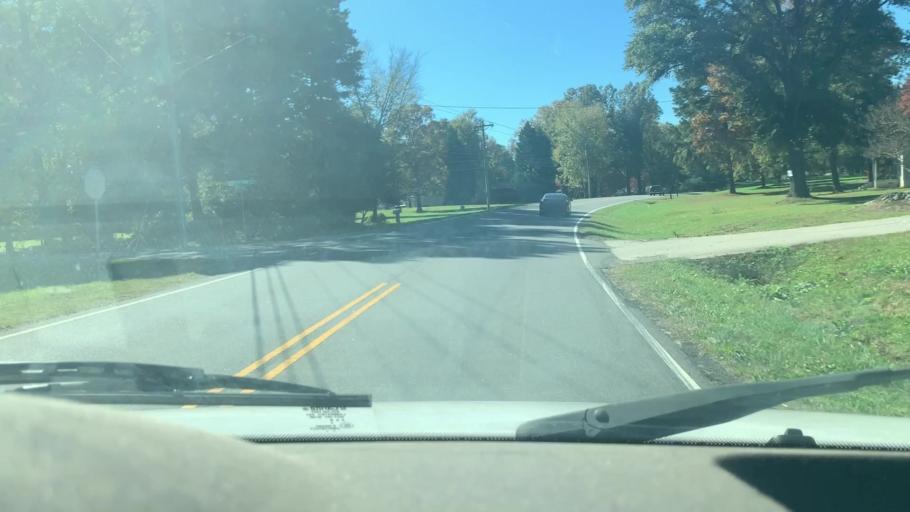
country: US
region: North Carolina
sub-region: Mecklenburg County
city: Huntersville
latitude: 35.4328
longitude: -80.9066
